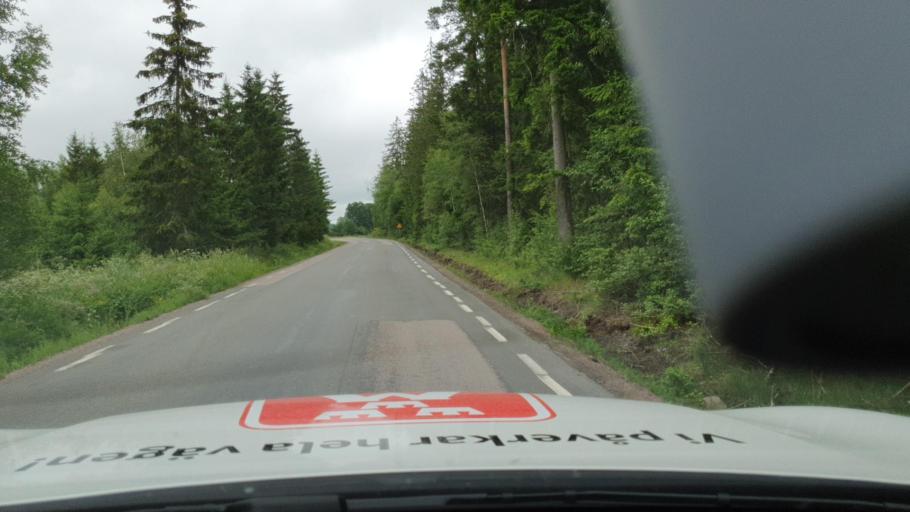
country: SE
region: Vaestra Goetaland
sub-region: Tibro Kommun
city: Tibro
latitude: 58.3899
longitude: 14.0643
